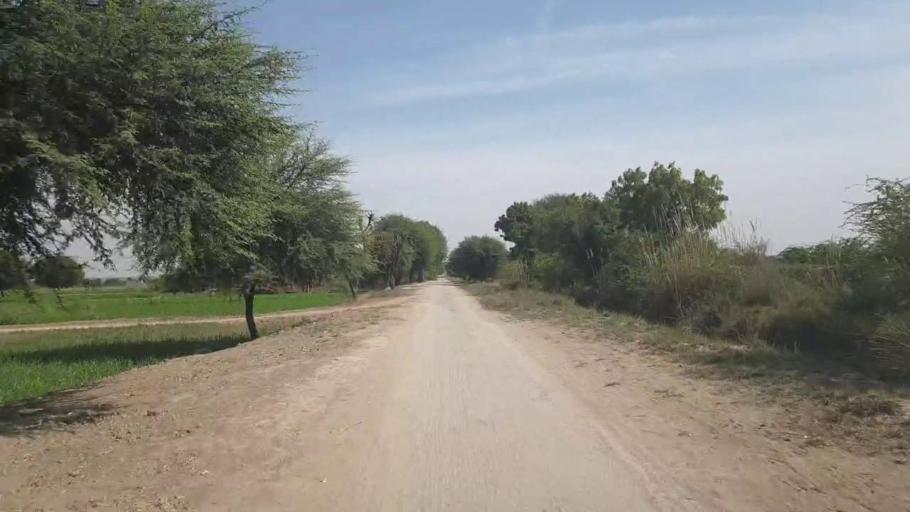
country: PK
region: Sindh
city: Kunri
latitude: 25.1906
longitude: 69.6840
